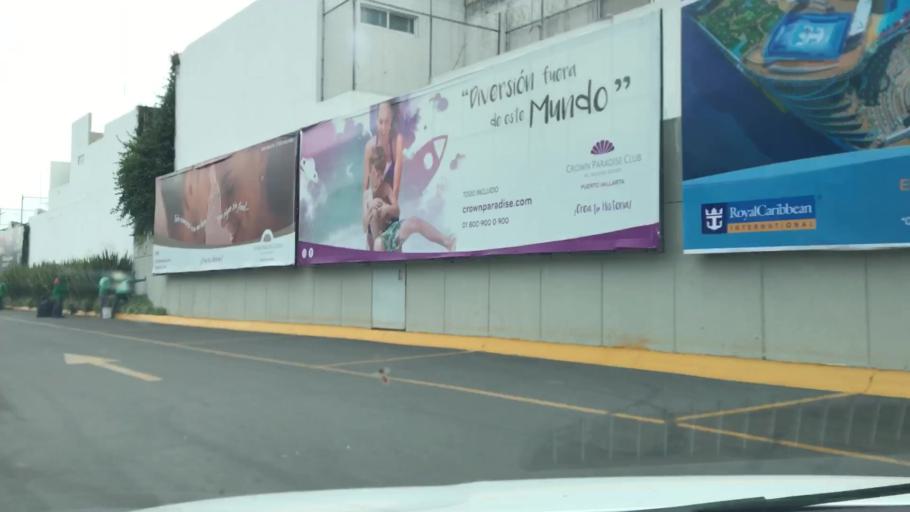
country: MX
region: Jalisco
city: Guadalajara
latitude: 20.6757
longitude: -103.4315
